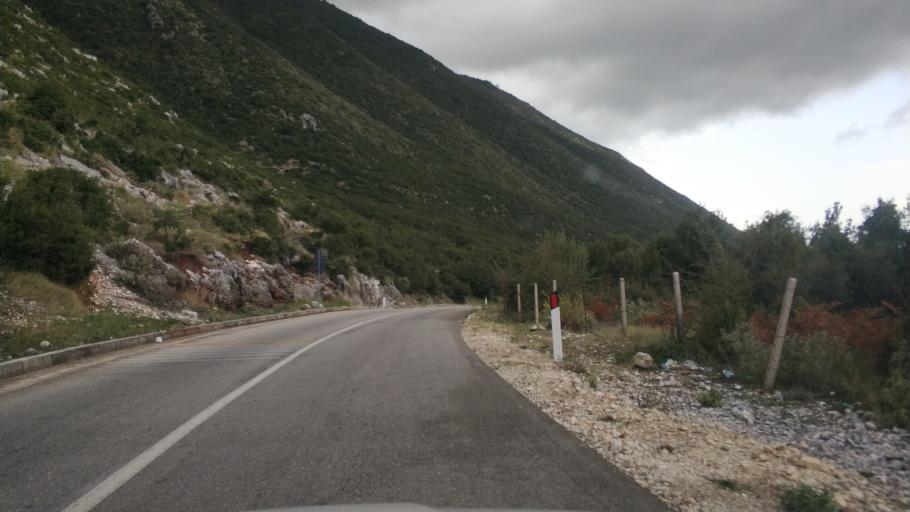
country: AL
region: Vlore
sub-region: Rrethi i Vlores
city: Brataj
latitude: 40.2326
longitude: 19.5584
